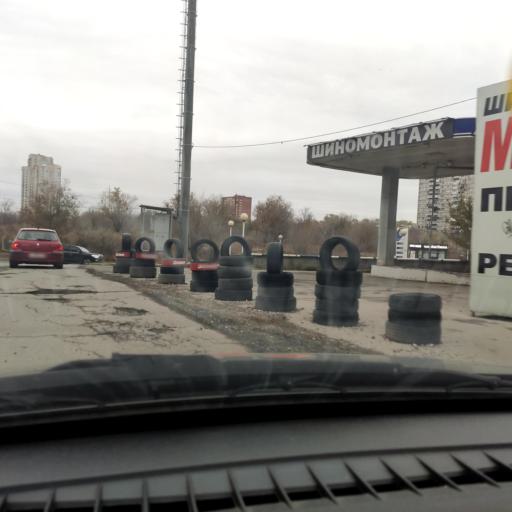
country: RU
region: Samara
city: Tol'yatti
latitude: 53.5081
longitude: 49.2527
